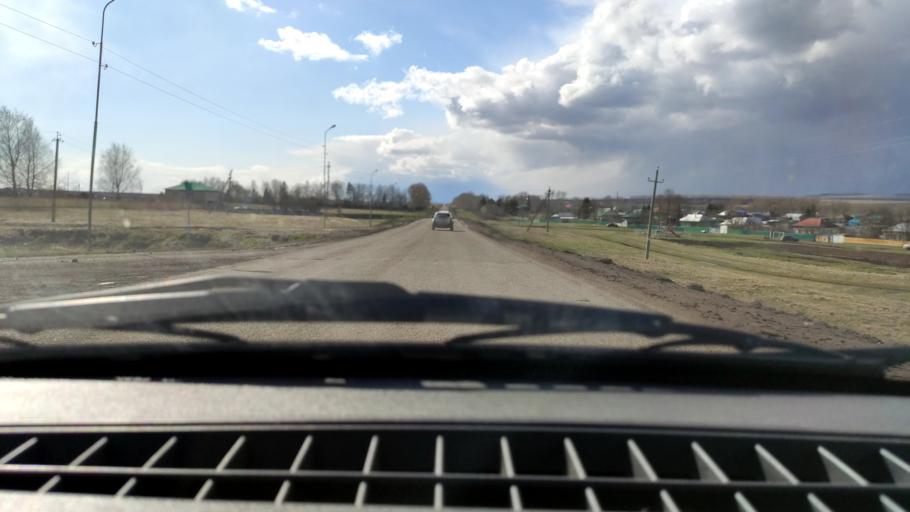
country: RU
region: Bashkortostan
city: Chekmagush
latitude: 55.1172
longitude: 54.8236
